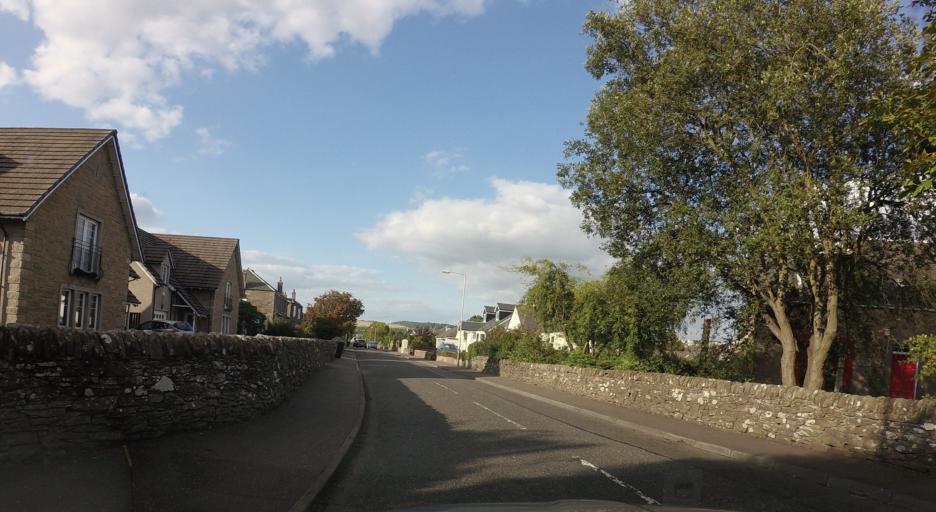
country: GB
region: Scotland
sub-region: Angus
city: Muirhead
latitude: 56.4561
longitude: -3.0629
